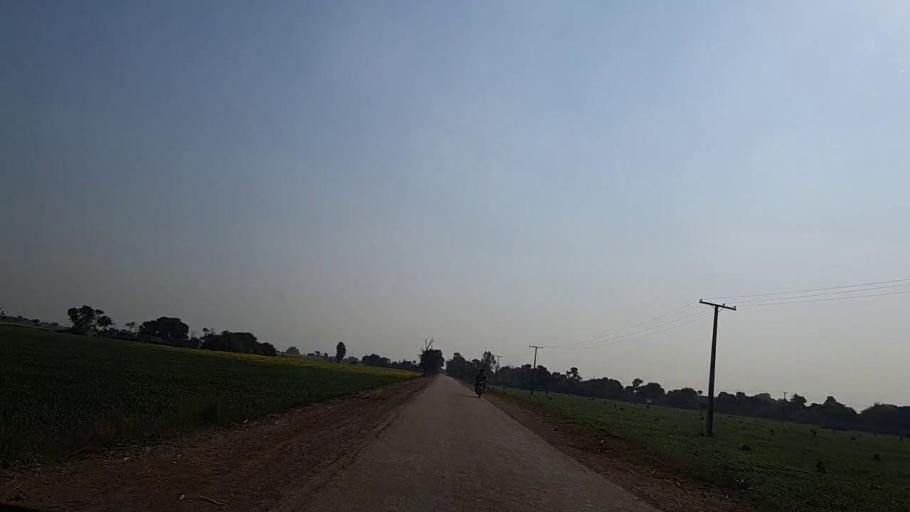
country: PK
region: Sindh
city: Sakrand
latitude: 26.0659
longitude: 68.2896
